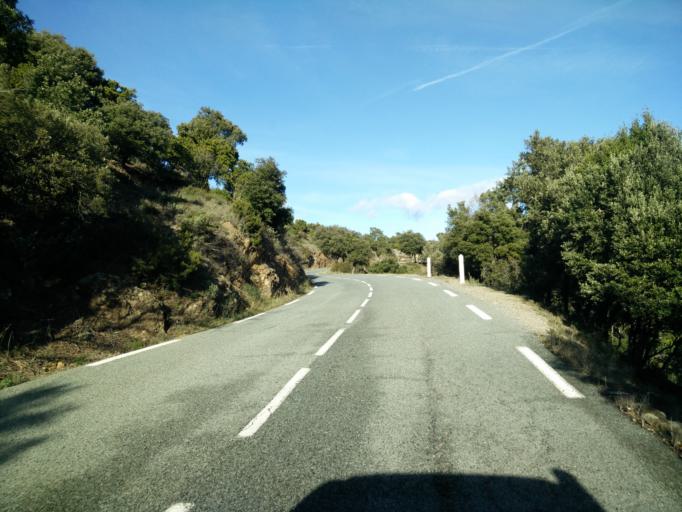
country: FR
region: Provence-Alpes-Cote d'Azur
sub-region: Departement du Var
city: Saint-Raphael
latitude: 43.4913
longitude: 6.7785
